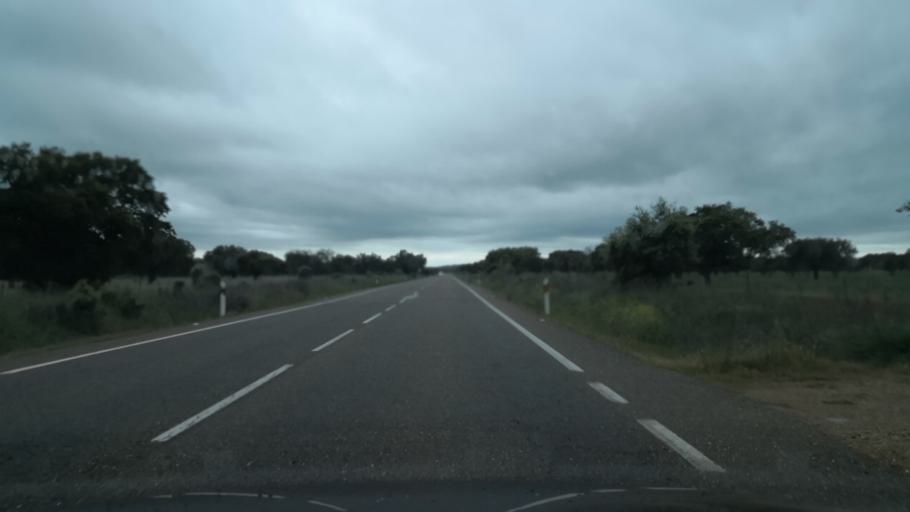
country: ES
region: Extremadura
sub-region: Provincia de Badajoz
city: La Roca de la Sierra
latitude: 39.0768
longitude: -6.7482
